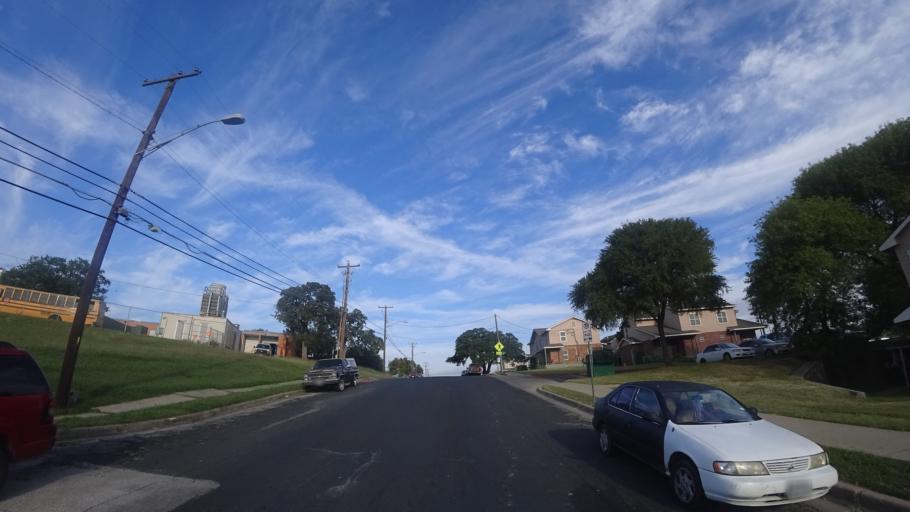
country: US
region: Texas
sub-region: Travis County
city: Austin
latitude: 30.2696
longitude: -97.7077
